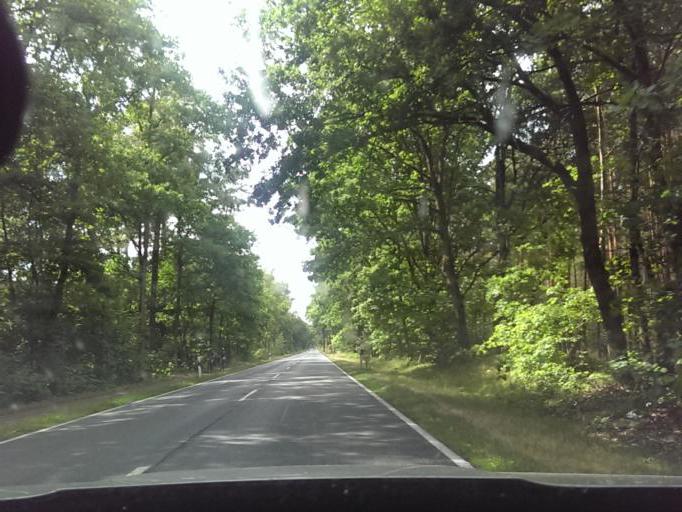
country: DE
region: Lower Saxony
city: Essel
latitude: 52.6969
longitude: 9.6732
